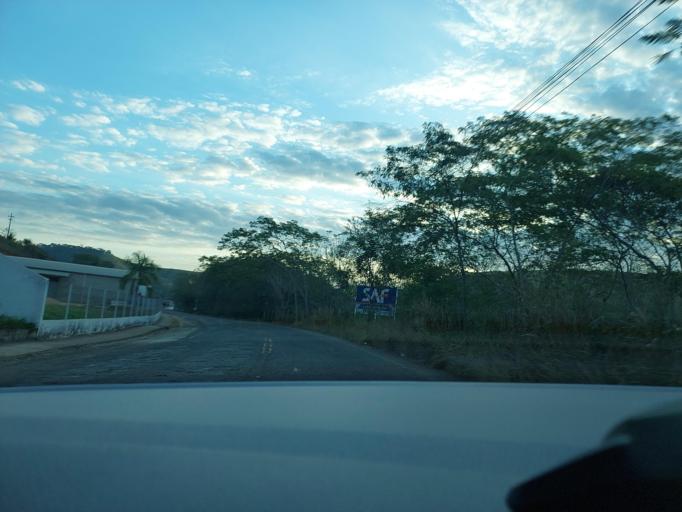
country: BR
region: Rio de Janeiro
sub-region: Natividade
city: Natividade
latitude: -21.1997
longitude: -42.1214
